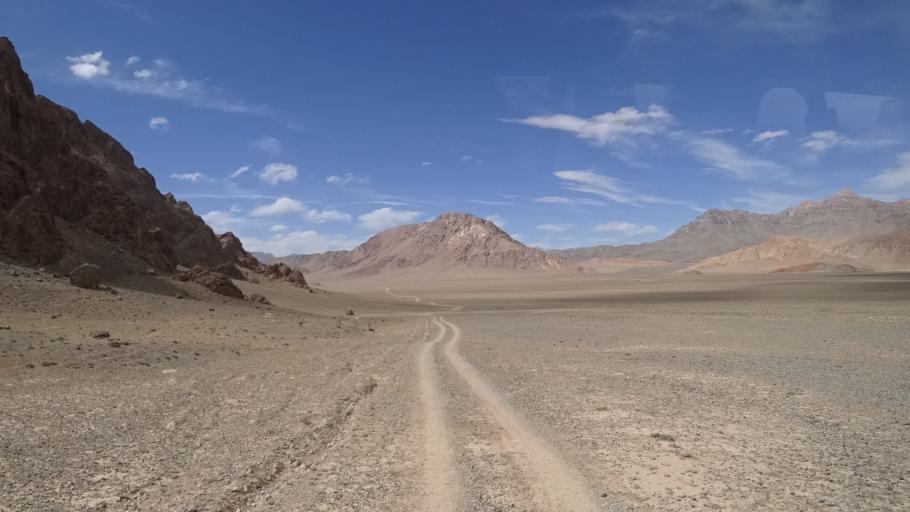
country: TJ
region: Gorno-Badakhshan
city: Murghob
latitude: 37.9091
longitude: 74.0188
